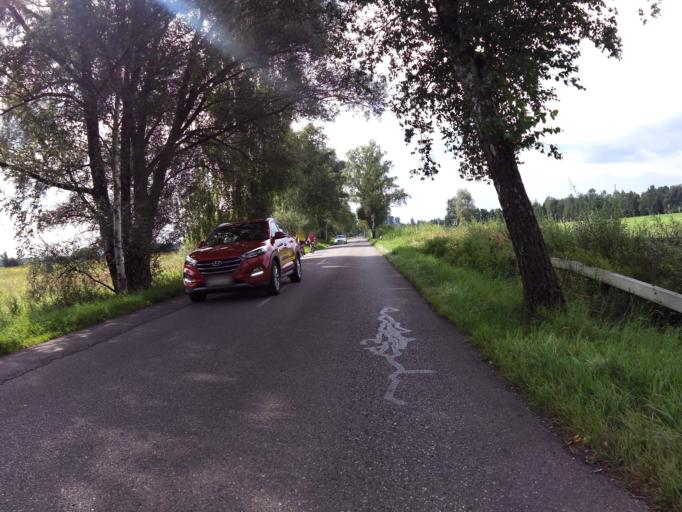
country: DE
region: Bavaria
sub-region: Upper Bavaria
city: Diessen am Ammersee
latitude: 47.9343
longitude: 11.1089
